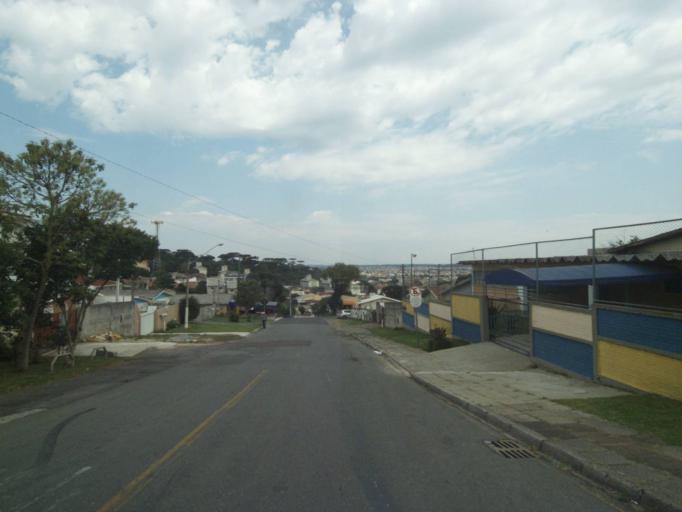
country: BR
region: Parana
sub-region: Sao Jose Dos Pinhais
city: Sao Jose dos Pinhais
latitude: -25.5248
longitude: -49.2562
